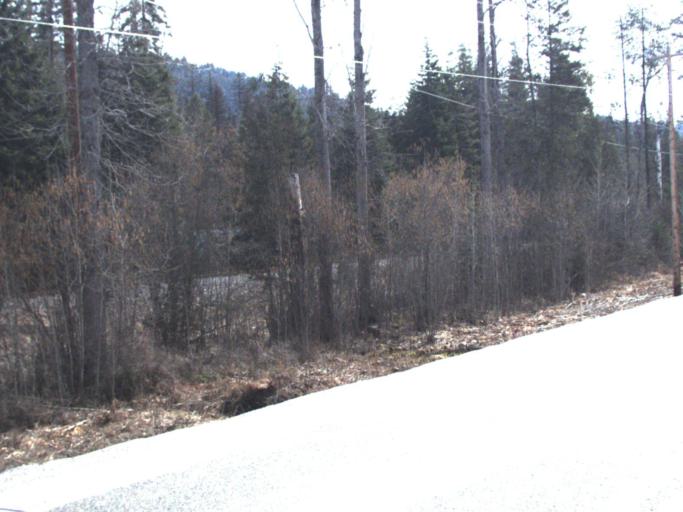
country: US
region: Washington
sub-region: Stevens County
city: Chewelah
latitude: 48.6000
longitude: -117.3605
